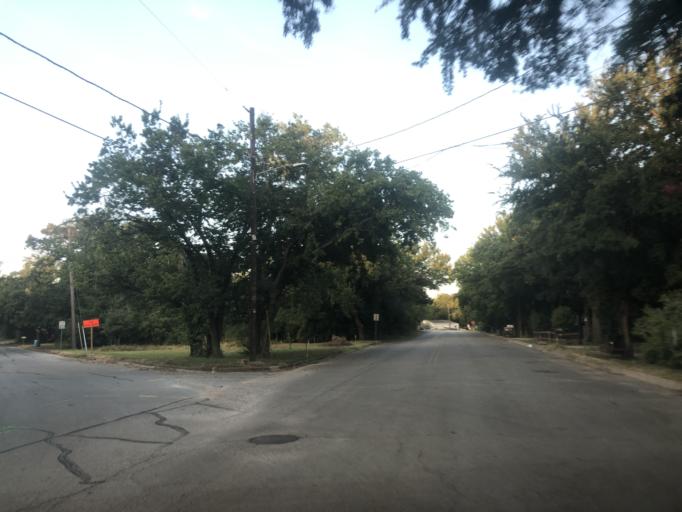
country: US
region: Texas
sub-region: Tarrant County
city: Lake Worth
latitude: 32.8061
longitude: -97.4496
